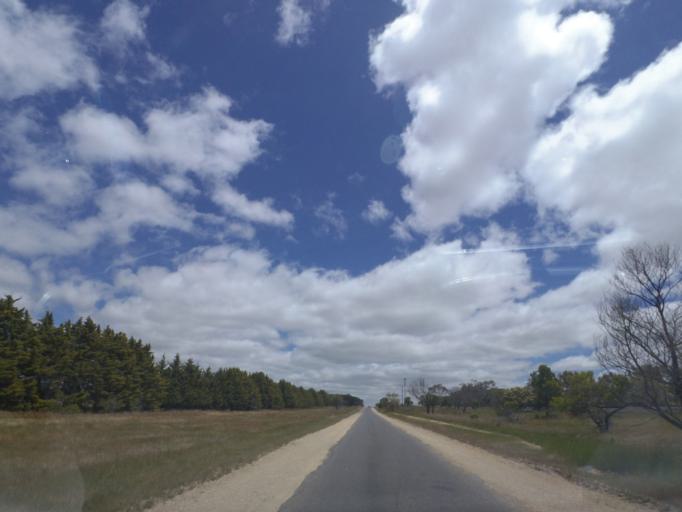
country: AU
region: Victoria
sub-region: Moorabool
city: Bacchus Marsh
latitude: -37.6366
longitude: 144.2761
